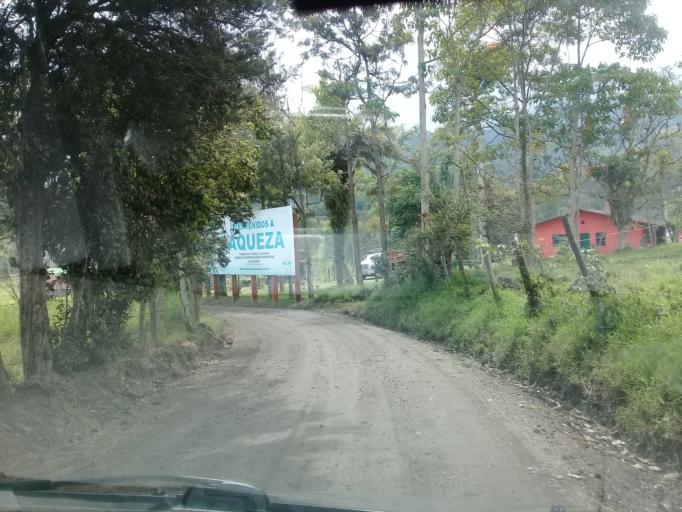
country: CO
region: Cundinamarca
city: Une
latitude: 4.4078
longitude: -73.9900
